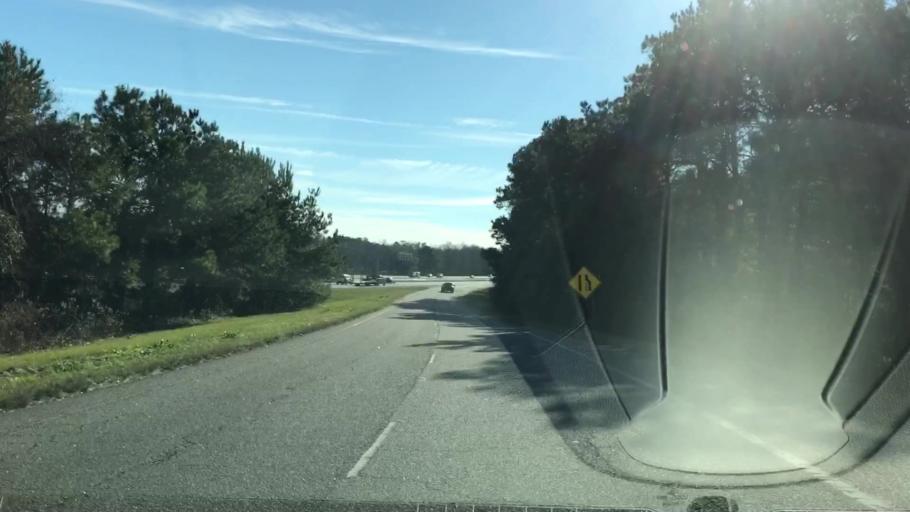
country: US
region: South Carolina
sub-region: Berkeley County
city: Ladson
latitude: 32.9975
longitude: -80.0937
